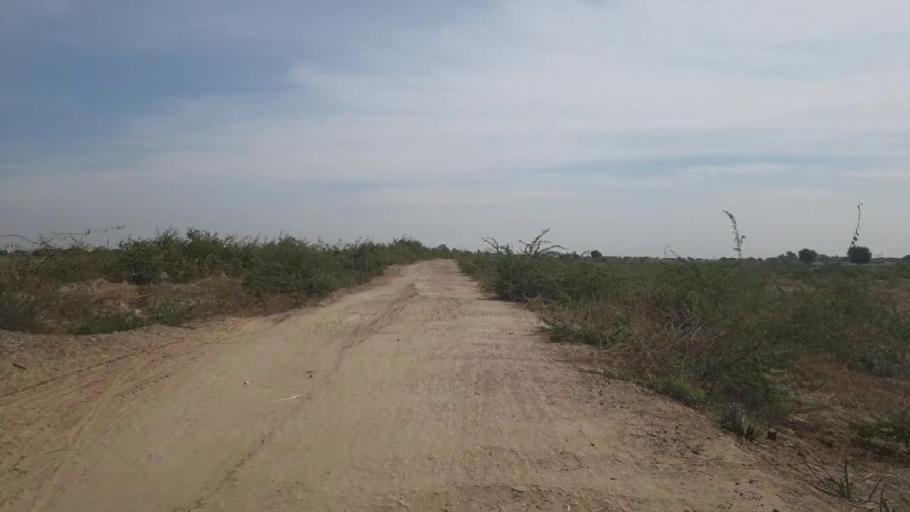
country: PK
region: Sindh
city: Kunri
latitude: 25.2902
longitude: 69.5878
